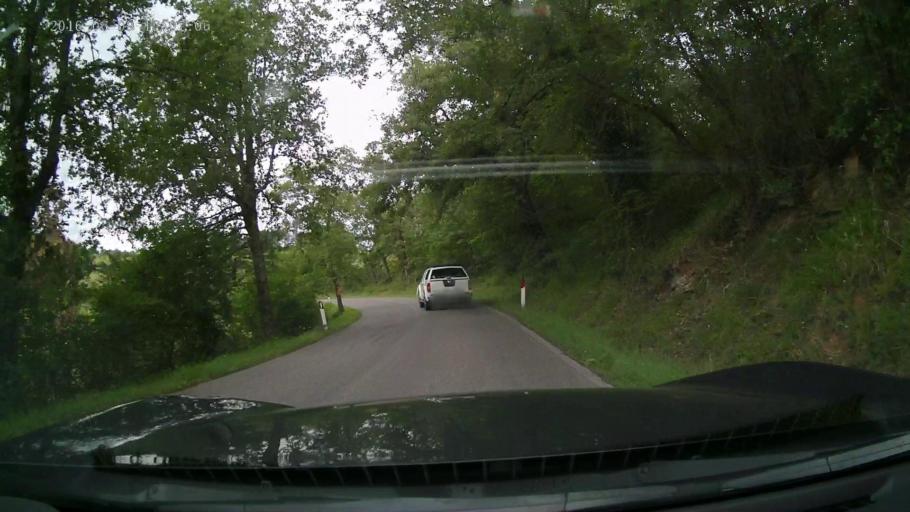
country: IT
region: Tuscany
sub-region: Province of Florence
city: Panzano in Chianti
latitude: 43.5273
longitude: 11.2862
